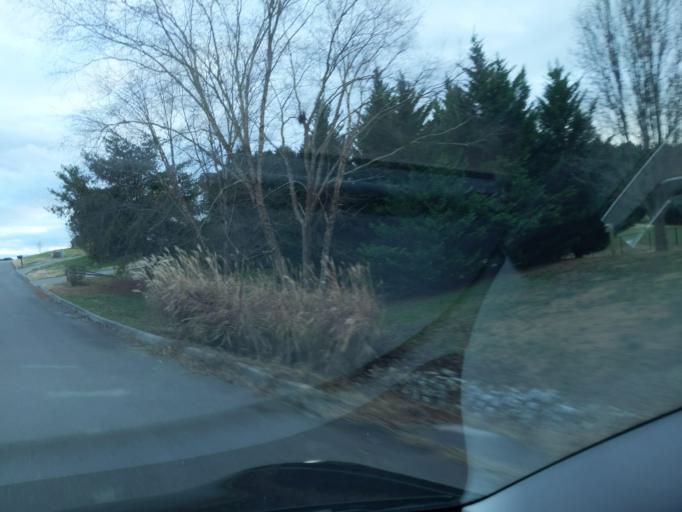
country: US
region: Tennessee
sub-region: Jefferson County
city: Dandridge
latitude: 35.9882
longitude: -83.4635
